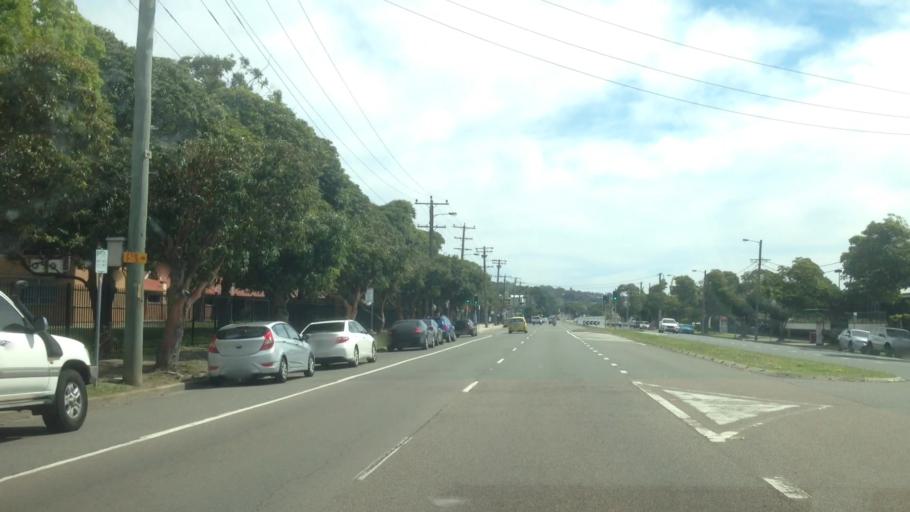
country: AU
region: New South Wales
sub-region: Newcastle
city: Broadmeadow
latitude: -32.9239
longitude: 151.7292
